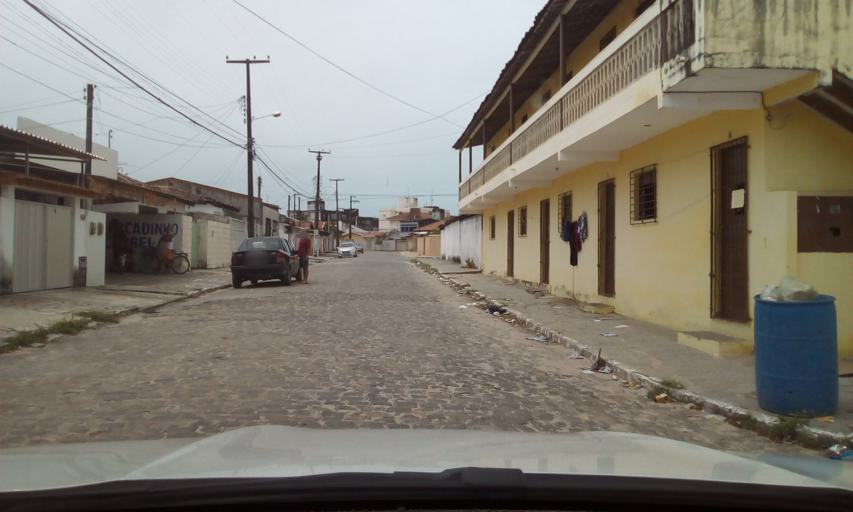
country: BR
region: Paraiba
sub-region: Joao Pessoa
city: Joao Pessoa
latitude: -7.1671
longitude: -34.8328
